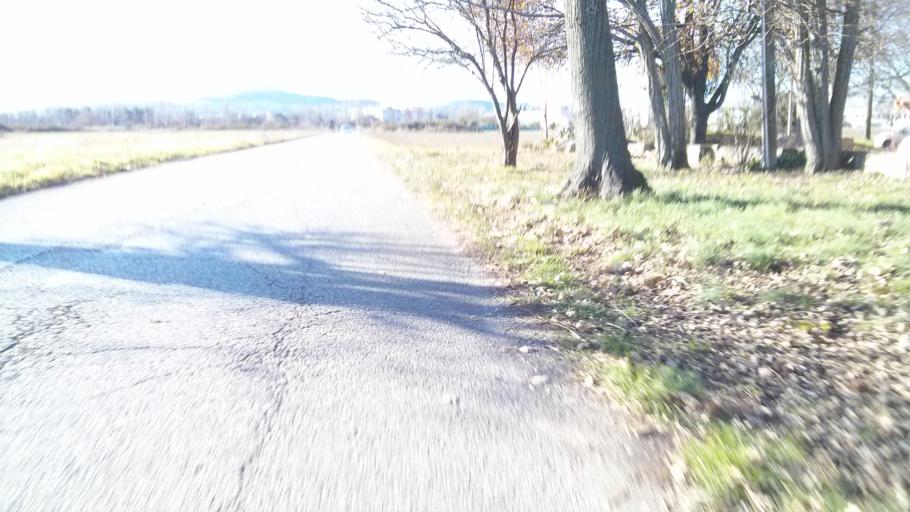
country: IT
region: The Marches
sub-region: Provincia di Pesaro e Urbino
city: Fano
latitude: 43.8292
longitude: 13.0225
